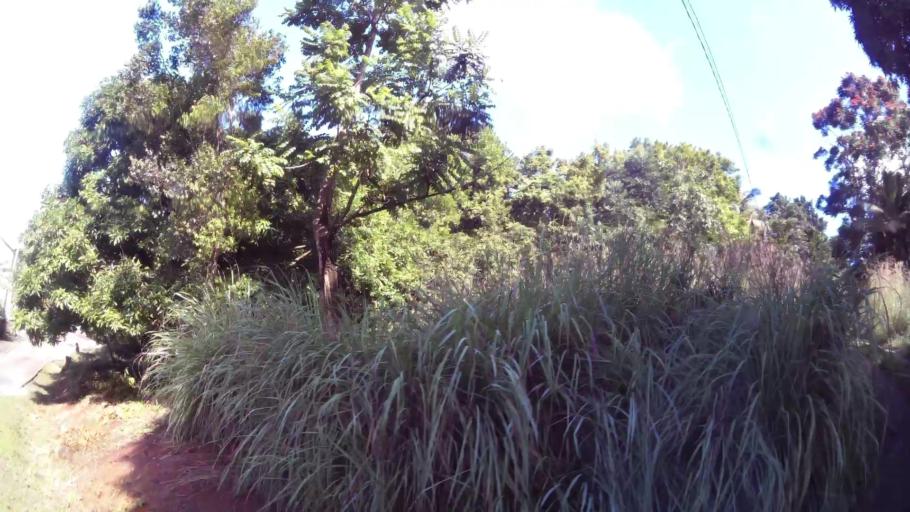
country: DM
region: Saint John
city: Portsmouth
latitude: 15.5528
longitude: -61.4558
